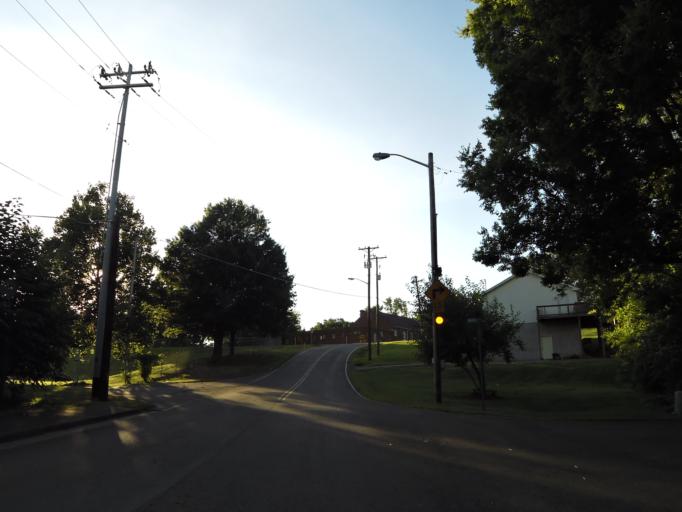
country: US
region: Tennessee
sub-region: Knox County
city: Knoxville
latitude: 35.9733
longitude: -83.9445
